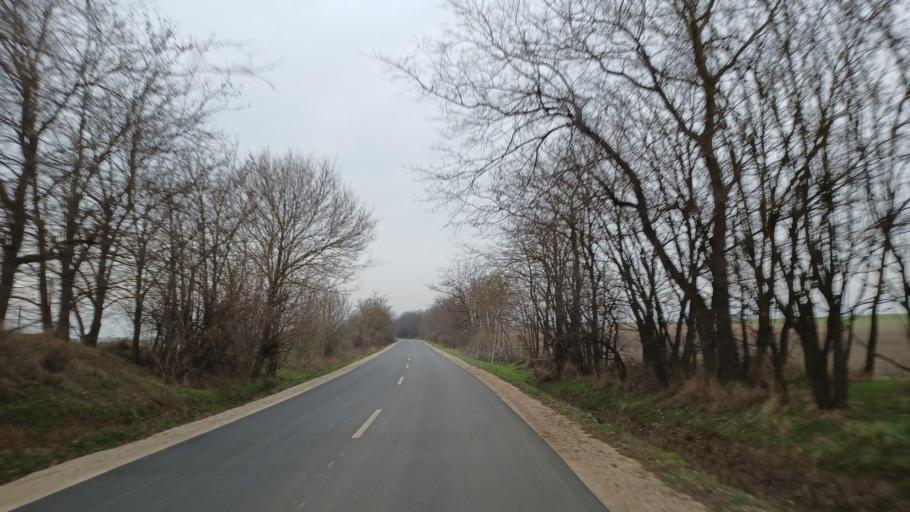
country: HU
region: Tolna
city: Nagydorog
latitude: 46.5725
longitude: 18.6328
